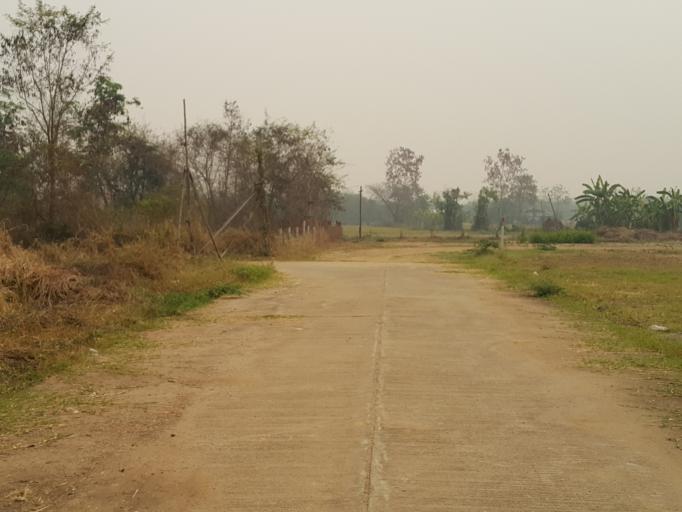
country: TH
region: Chiang Mai
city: San Kamphaeng
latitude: 18.7639
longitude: 99.0999
